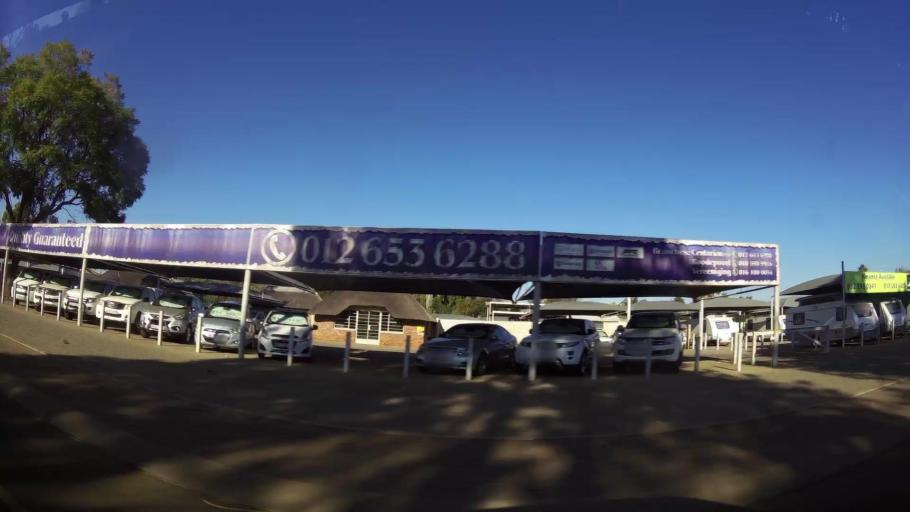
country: ZA
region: Gauteng
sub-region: City of Tshwane Metropolitan Municipality
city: Centurion
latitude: -25.8657
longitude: 28.1567
